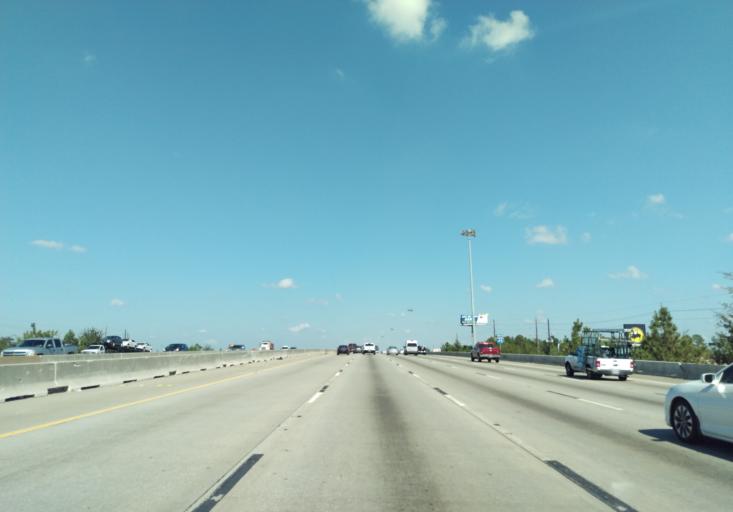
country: US
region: Texas
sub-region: Harris County
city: Aldine
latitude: 29.9954
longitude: -95.4248
